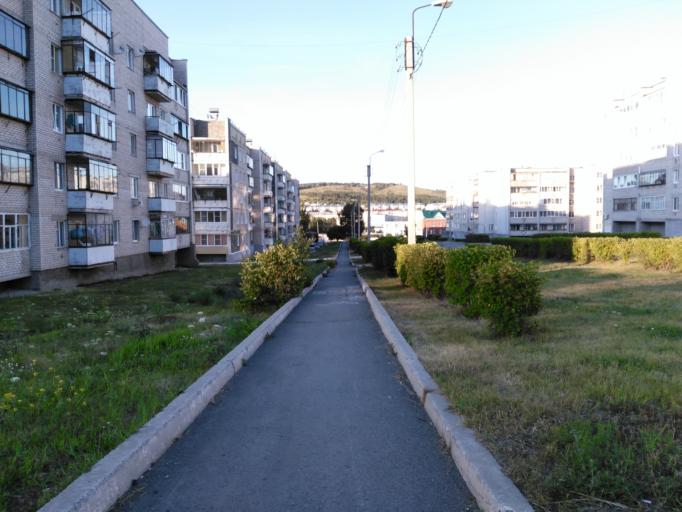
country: RU
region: Bashkortostan
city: Uchaly
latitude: 54.3185
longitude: 59.3687
